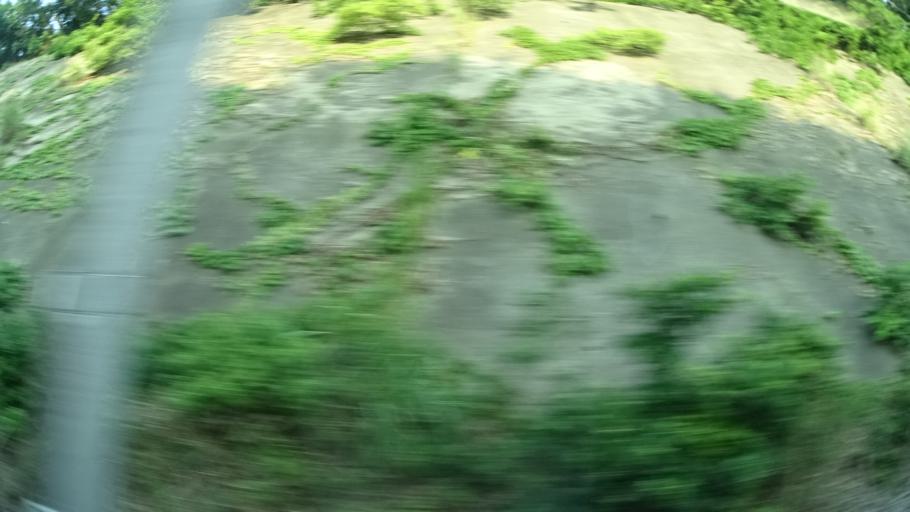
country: JP
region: Ibaraki
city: Funaishikawa
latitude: 36.4952
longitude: 140.6097
